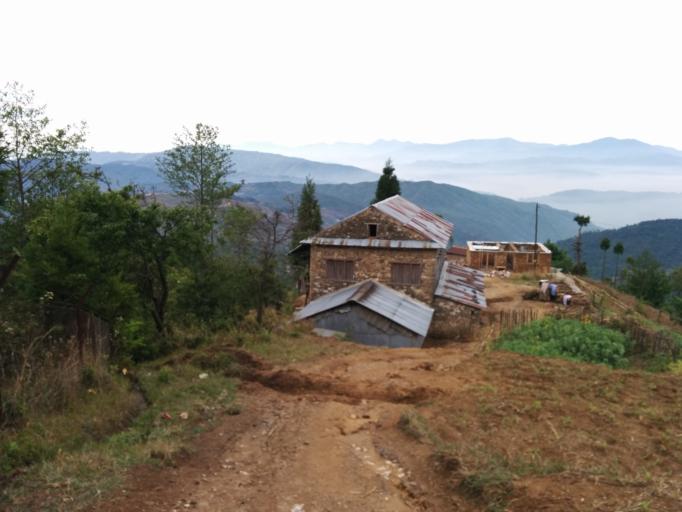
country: NP
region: Central Region
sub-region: Bagmati Zone
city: Nagarkot
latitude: 27.7768
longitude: 85.4910
